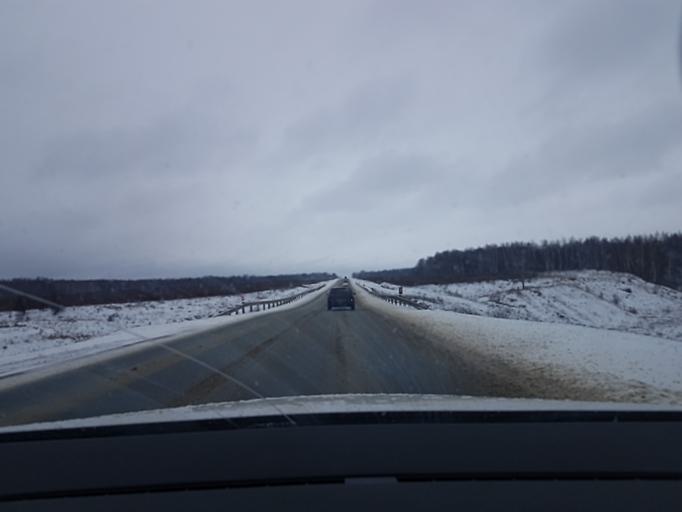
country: RU
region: Rjazan
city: Zarechnyy
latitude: 53.7751
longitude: 39.7285
